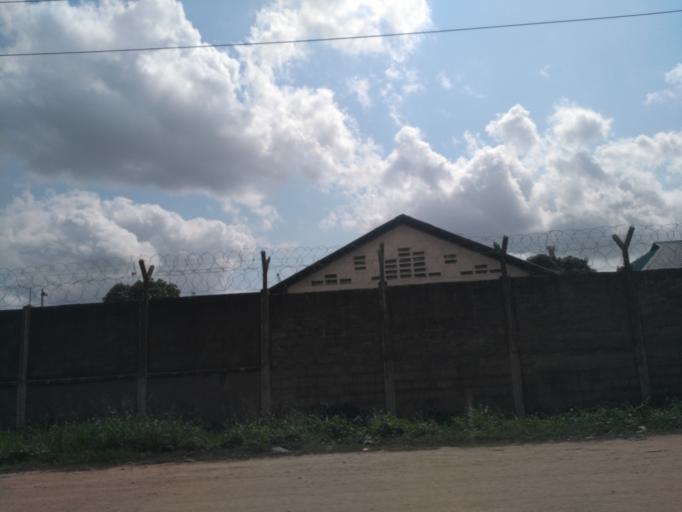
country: TZ
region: Dar es Salaam
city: Dar es Salaam
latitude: -6.8368
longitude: 39.2912
